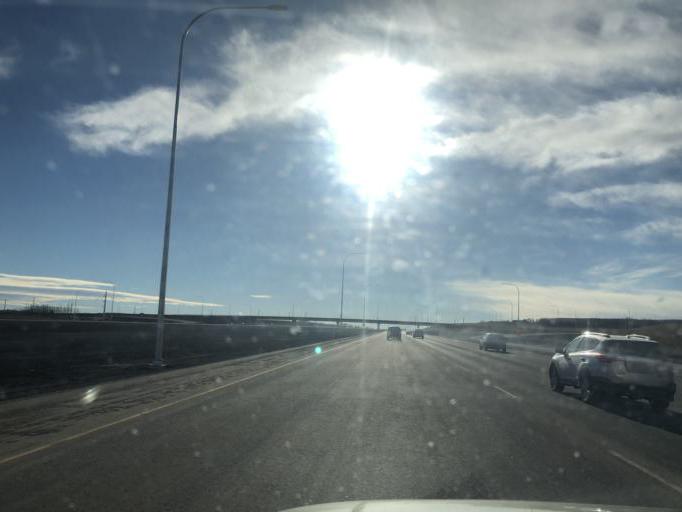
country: CA
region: Alberta
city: Calgary
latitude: 50.9803
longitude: -114.1616
